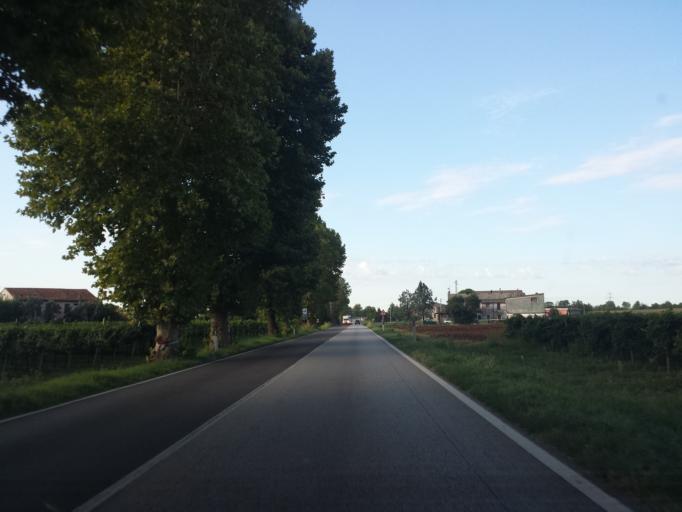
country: IT
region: Veneto
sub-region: Provincia di Vicenza
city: Montebello Vicentino
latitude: 45.4696
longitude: 11.4079
